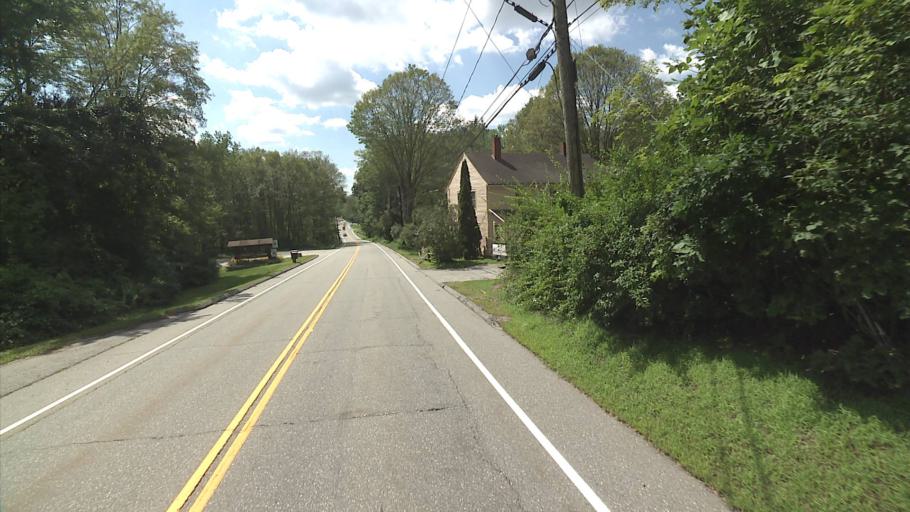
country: US
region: Connecticut
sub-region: Windham County
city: Windham
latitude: 41.8310
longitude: -72.0973
